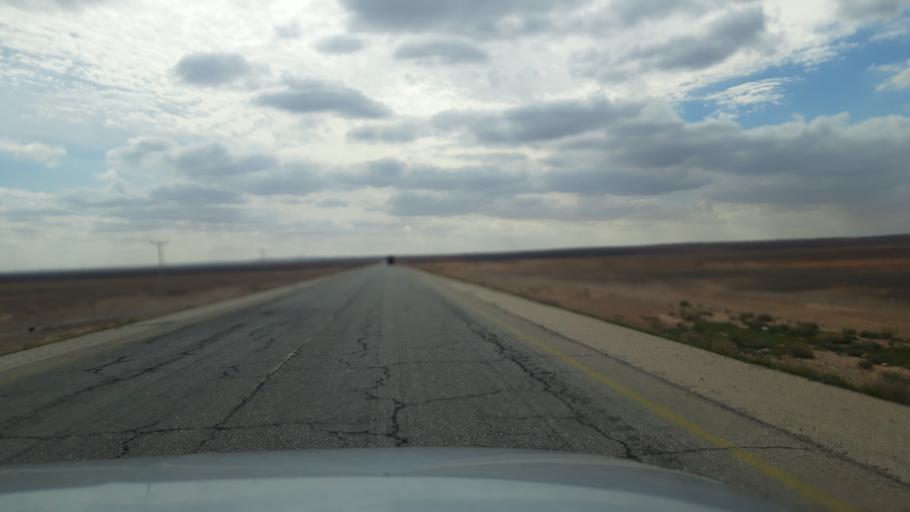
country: JO
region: Amman
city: Al Azraq ash Shamali
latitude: 31.8255
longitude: 36.6141
